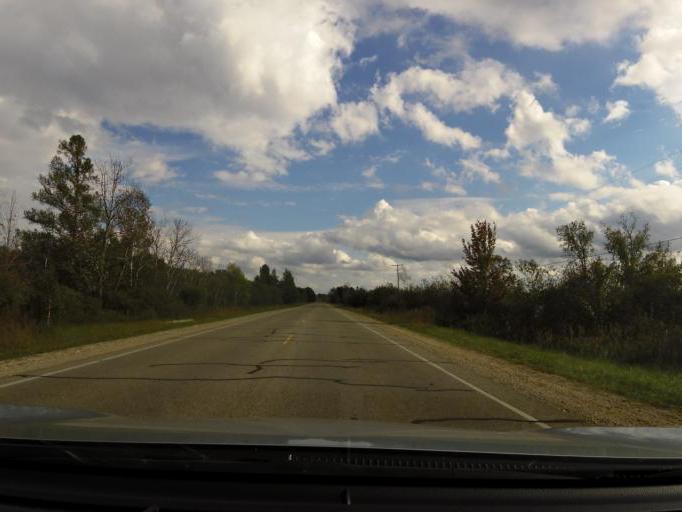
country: US
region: Michigan
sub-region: Roscommon County
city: Saint Helen
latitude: 44.4017
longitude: -84.4444
